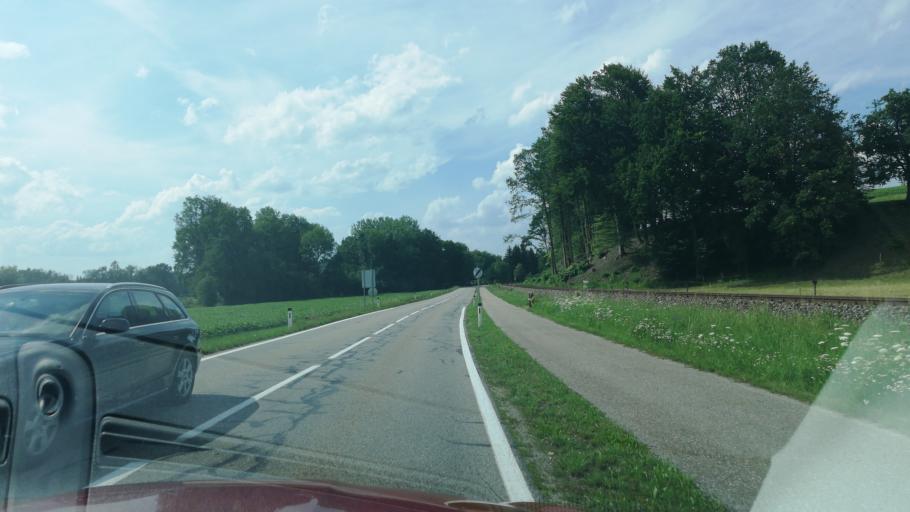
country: AT
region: Upper Austria
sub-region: Politischer Bezirk Vocklabruck
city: Puhret
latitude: 48.0241
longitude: 13.7084
